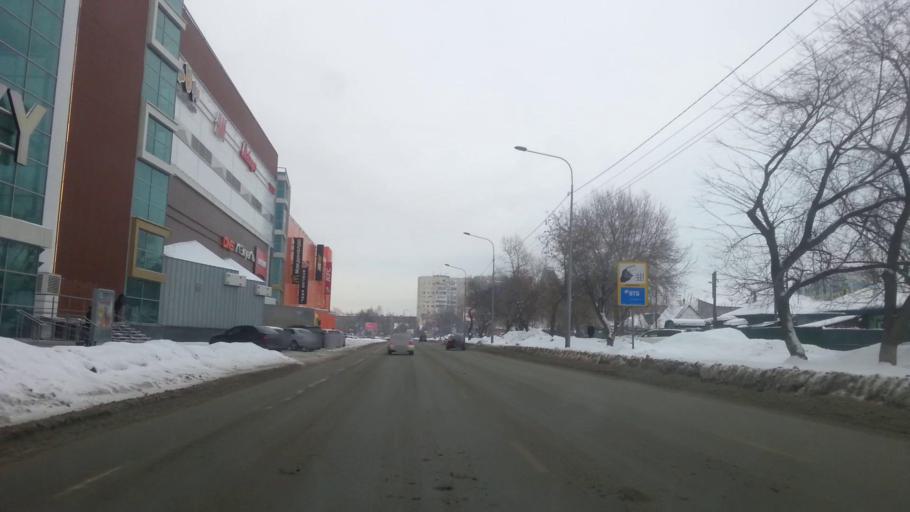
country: RU
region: Altai Krai
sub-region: Gorod Barnaulskiy
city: Barnaul
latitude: 53.3412
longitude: 83.7509
